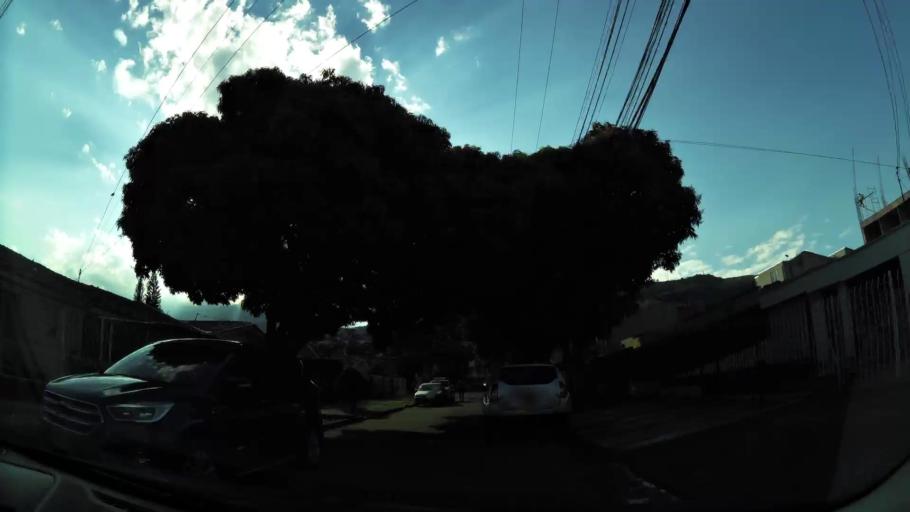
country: CO
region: Valle del Cauca
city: Cali
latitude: 3.4197
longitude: -76.5497
